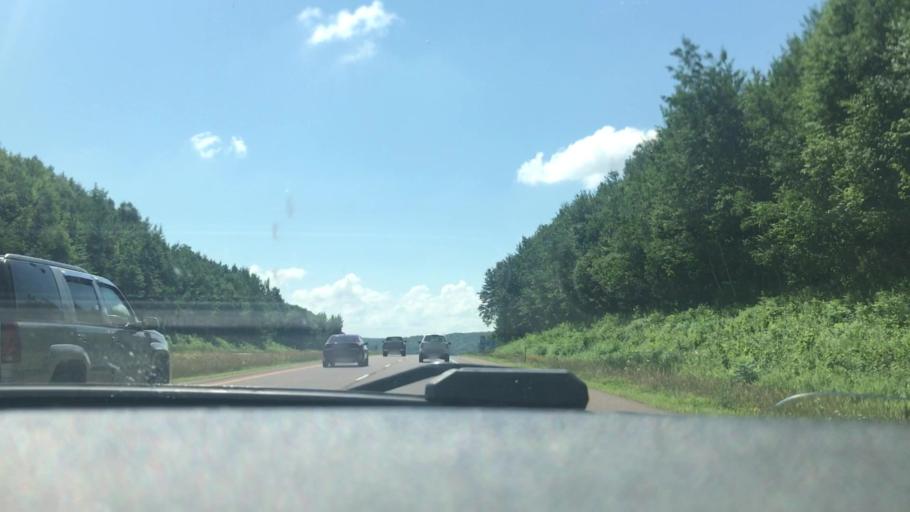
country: US
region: Wisconsin
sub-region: Chippewa County
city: Chippewa Falls
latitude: 44.9760
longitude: -91.4353
